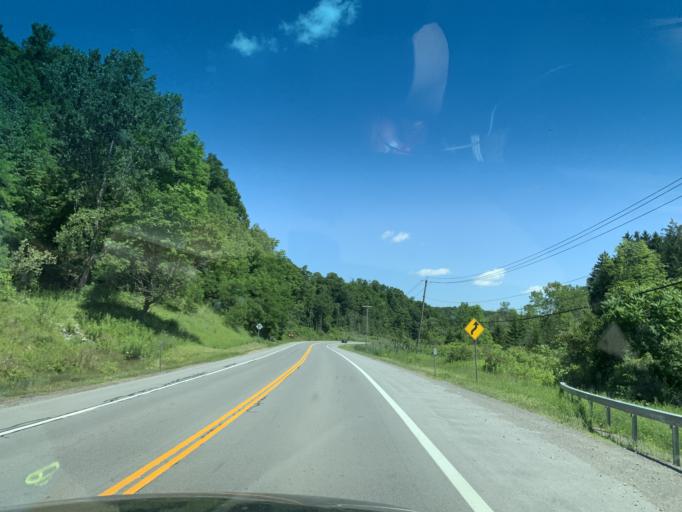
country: US
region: New York
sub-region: Oneida County
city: Chadwicks
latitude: 42.9481
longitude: -75.2449
